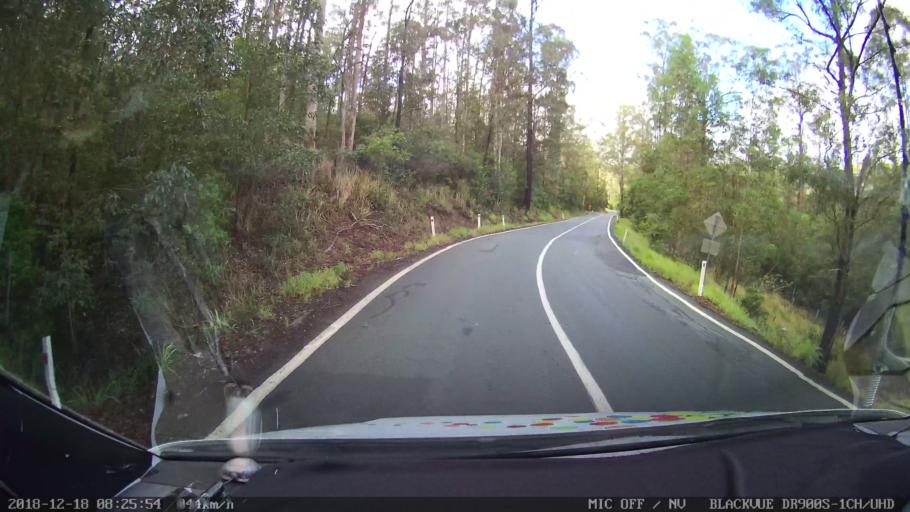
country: AU
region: New South Wales
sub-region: Kyogle
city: Kyogle
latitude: -28.3243
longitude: 152.7410
